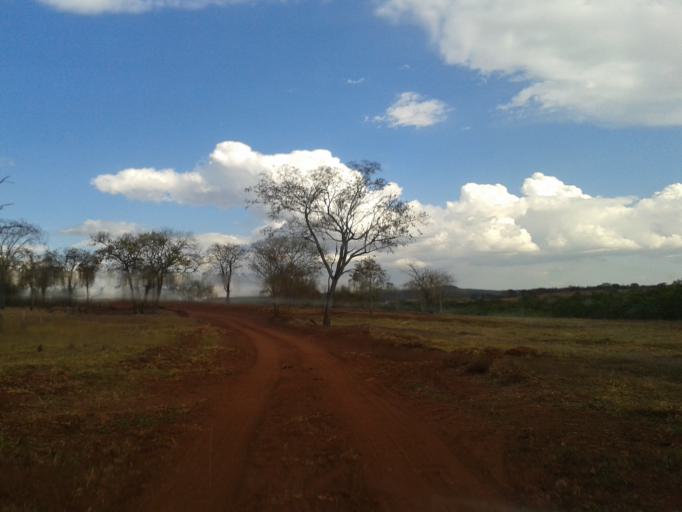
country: BR
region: Minas Gerais
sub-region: Santa Vitoria
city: Santa Vitoria
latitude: -19.1693
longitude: -49.9532
